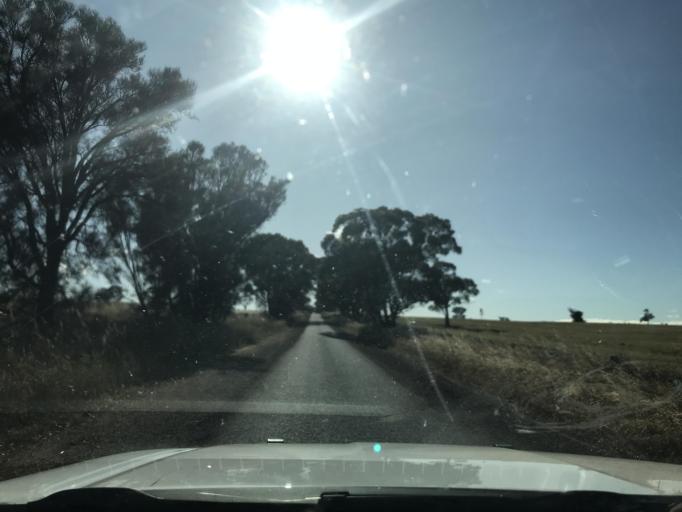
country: AU
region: Victoria
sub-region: Horsham
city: Horsham
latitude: -36.6978
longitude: 141.6021
